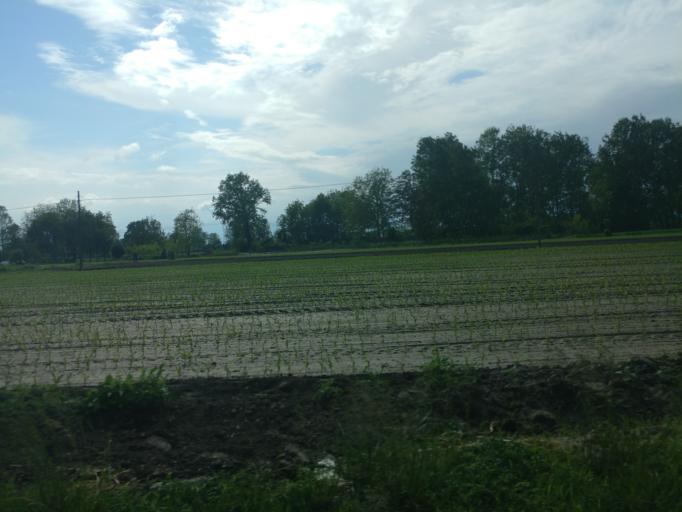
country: IT
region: Piedmont
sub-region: Provincia di Torino
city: Pancalieri
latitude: 44.8250
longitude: 7.5874
